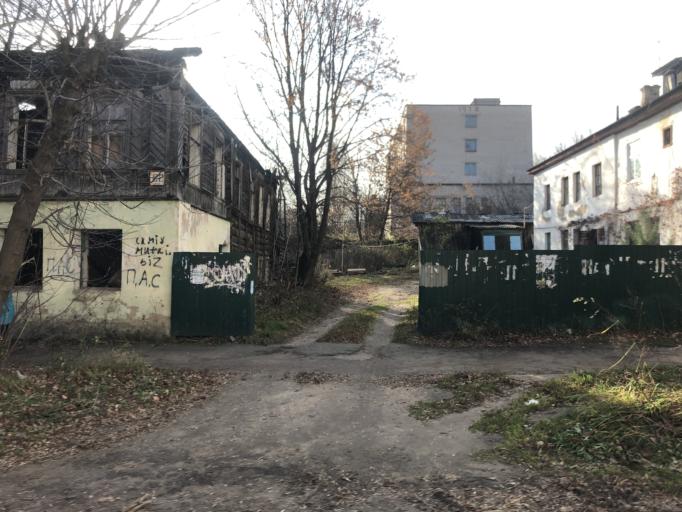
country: RU
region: Tverskaya
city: Rzhev
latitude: 56.2584
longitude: 34.3307
